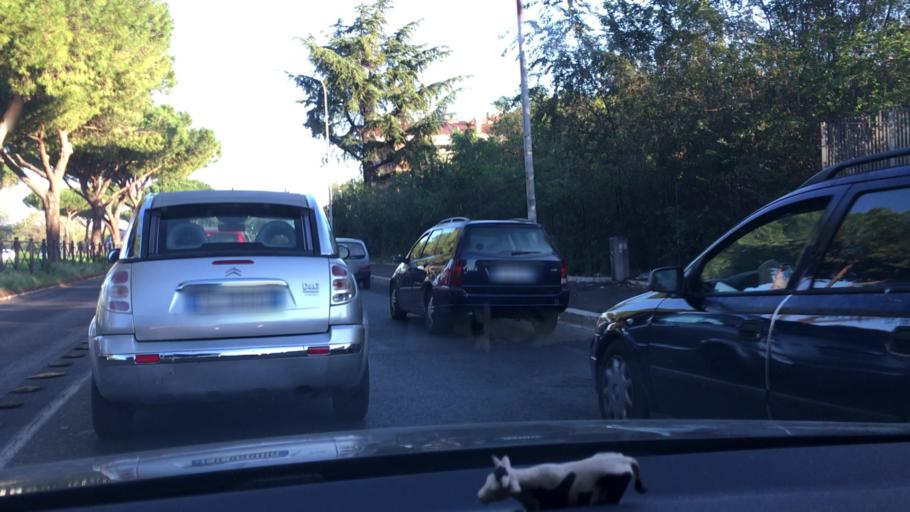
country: IT
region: Latium
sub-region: Citta metropolitana di Roma Capitale
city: Rome
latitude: 41.8631
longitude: 12.5690
